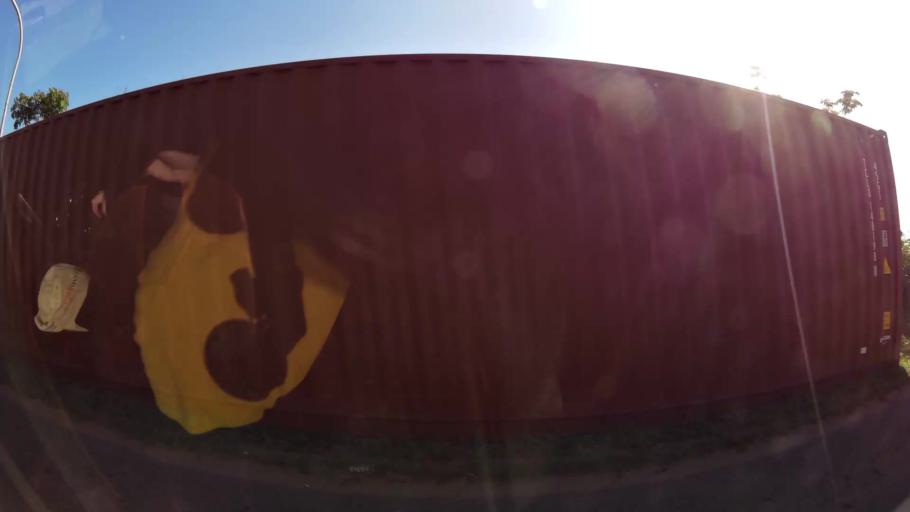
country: GF
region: Guyane
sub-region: Guyane
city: Matoury
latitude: 4.8618
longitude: -52.2768
